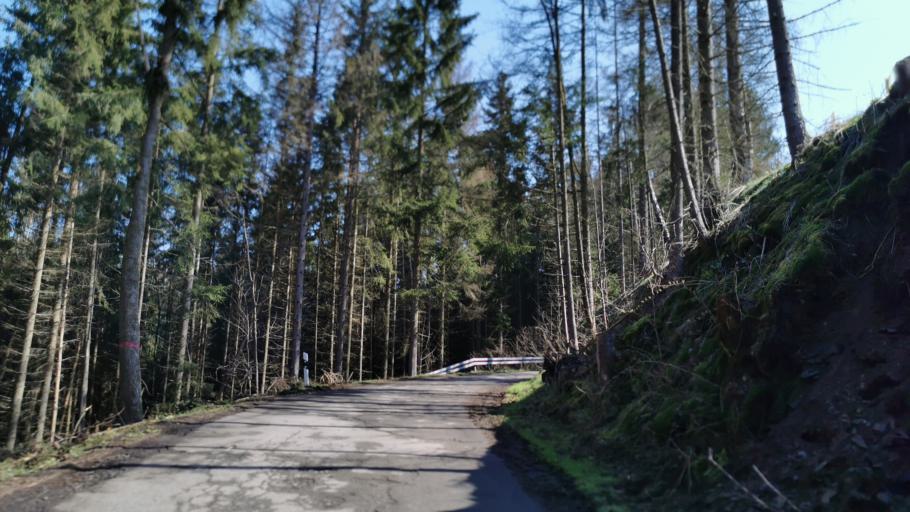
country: DE
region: Thuringia
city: Probstzella
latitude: 50.5135
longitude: 11.4124
